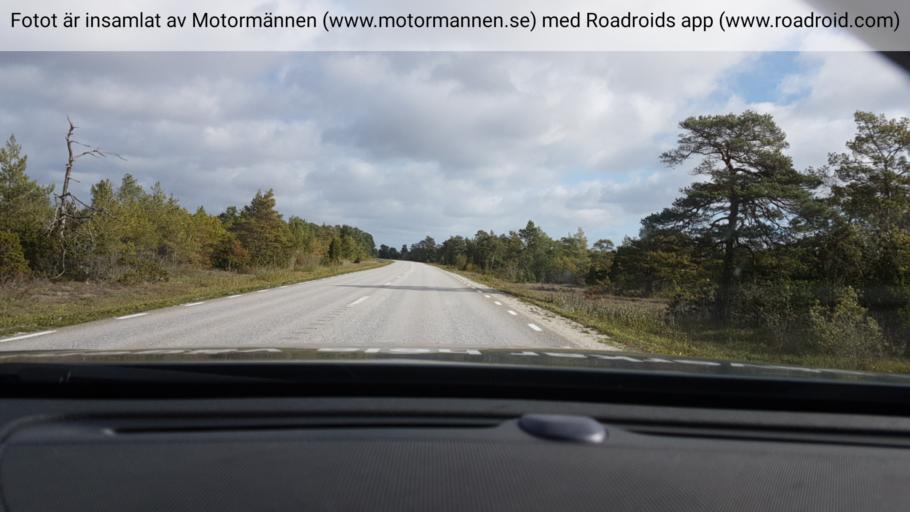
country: SE
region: Gotland
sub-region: Gotland
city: Slite
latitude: 57.8407
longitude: 18.9562
